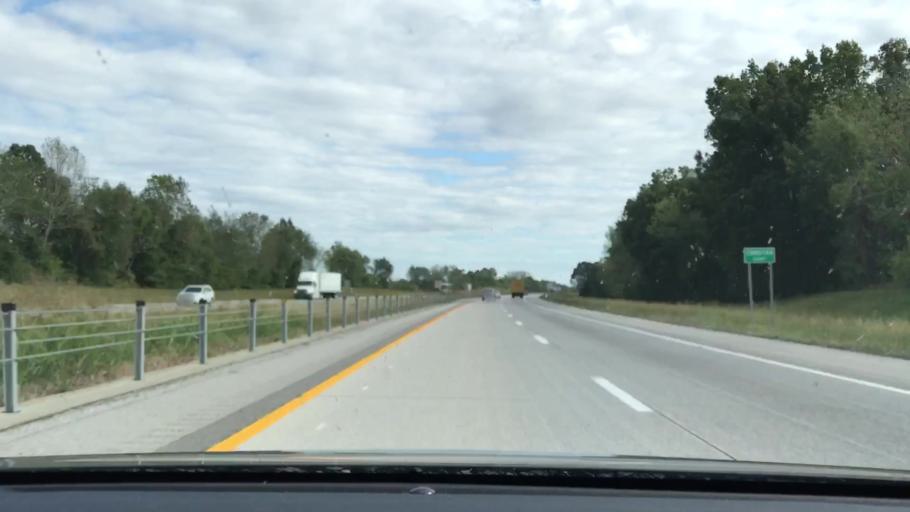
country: US
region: Kentucky
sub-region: Trigg County
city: Cadiz
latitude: 36.8423
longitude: -87.6742
